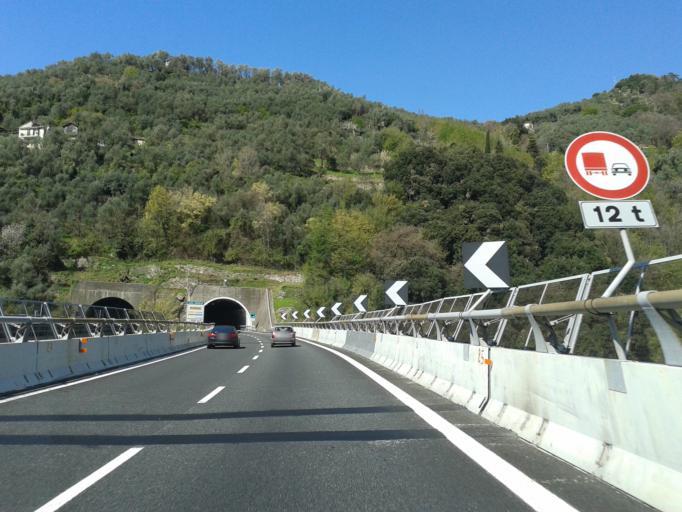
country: IT
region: Liguria
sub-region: Provincia di Genova
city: Rapallo
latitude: 44.3593
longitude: 9.2349
